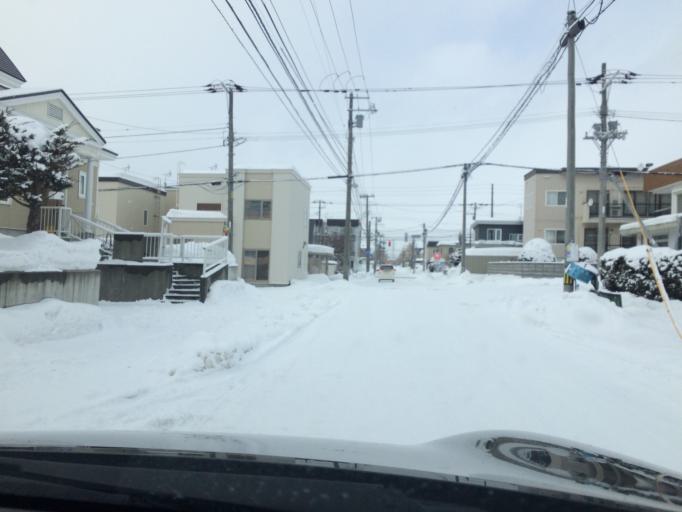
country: JP
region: Hokkaido
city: Ebetsu
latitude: 43.0496
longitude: 141.4684
